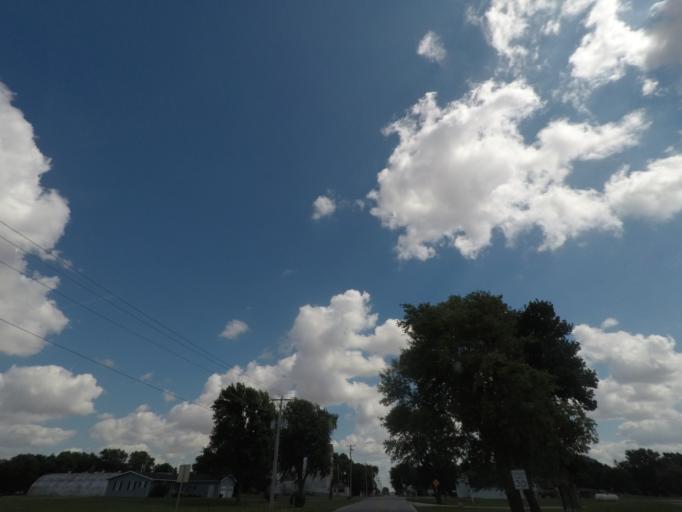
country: US
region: Iowa
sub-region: Story County
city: Nevada
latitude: 42.0706
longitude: -93.3980
